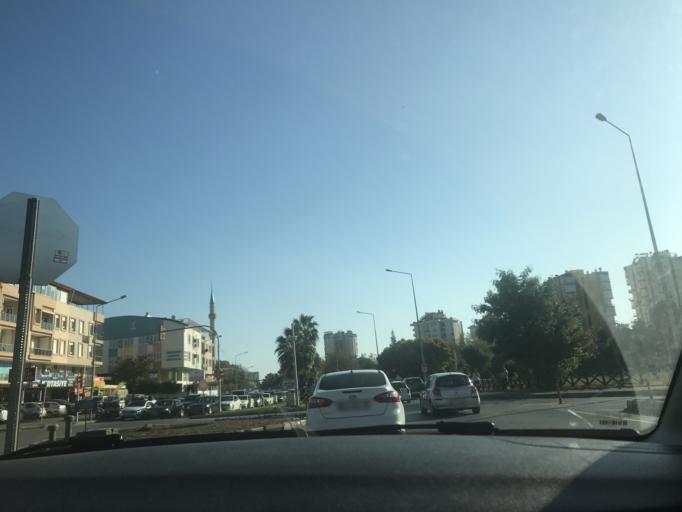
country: TR
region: Antalya
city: Antalya
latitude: 36.8839
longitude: 30.6482
